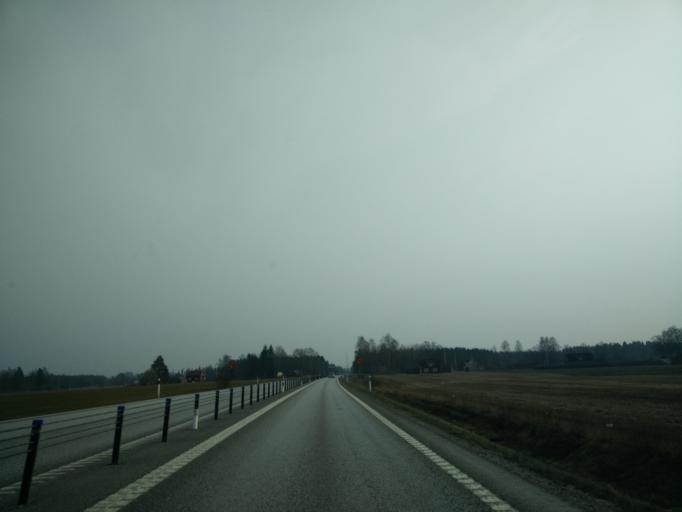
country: SE
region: Vaermland
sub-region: Forshaga Kommun
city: Forshaga
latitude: 59.4615
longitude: 13.4165
